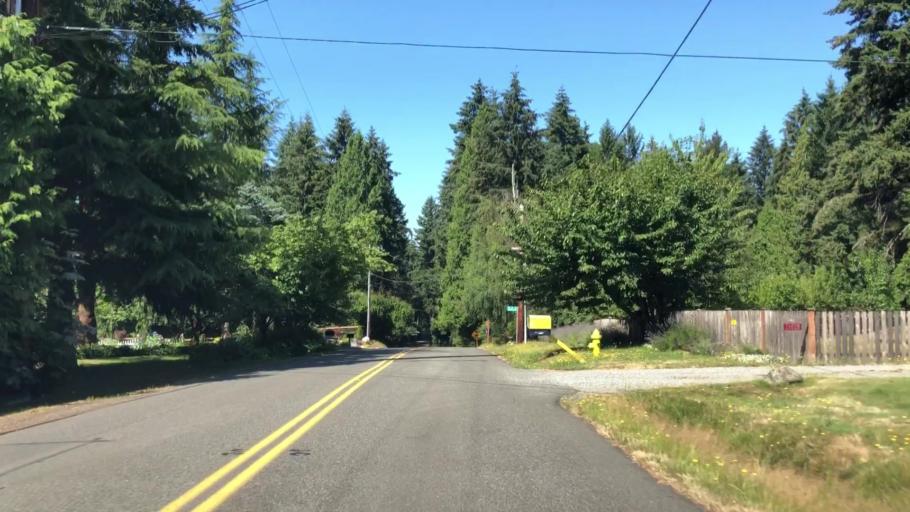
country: US
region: Washington
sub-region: King County
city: Woodinville
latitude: 47.7473
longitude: -122.1258
